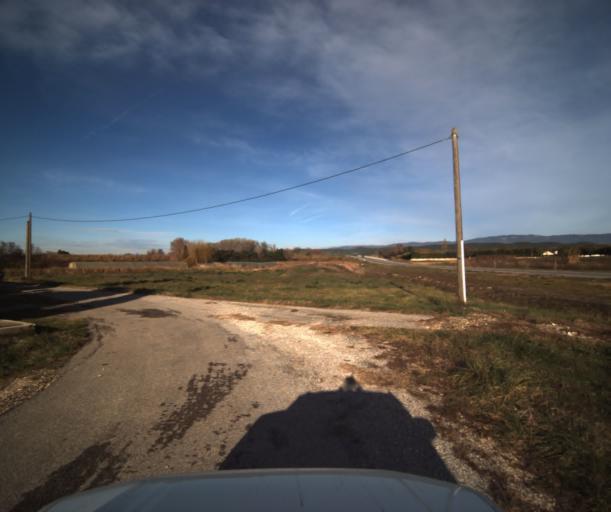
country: FR
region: Provence-Alpes-Cote d'Azur
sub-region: Departement du Vaucluse
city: Pertuis
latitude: 43.6805
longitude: 5.4868
